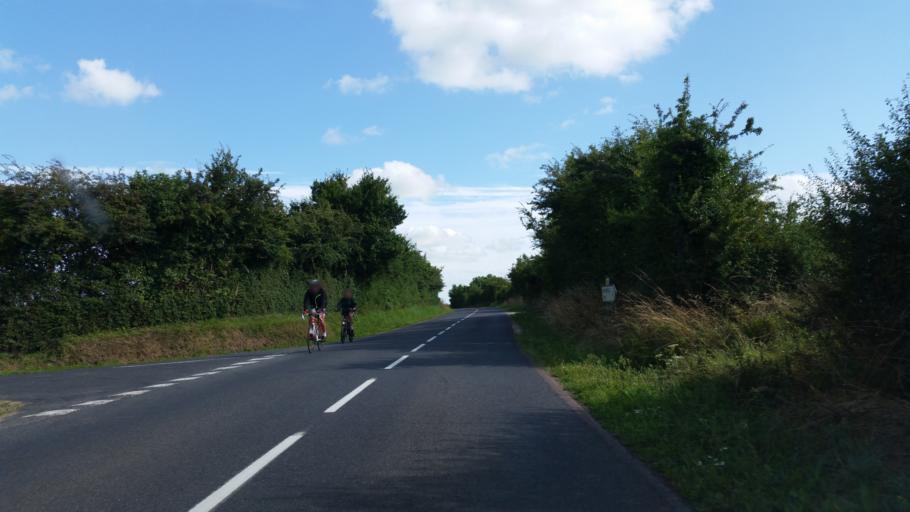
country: FR
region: Lower Normandy
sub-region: Departement de la Manche
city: Sainte-Mere-Eglise
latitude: 49.4470
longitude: -1.2603
